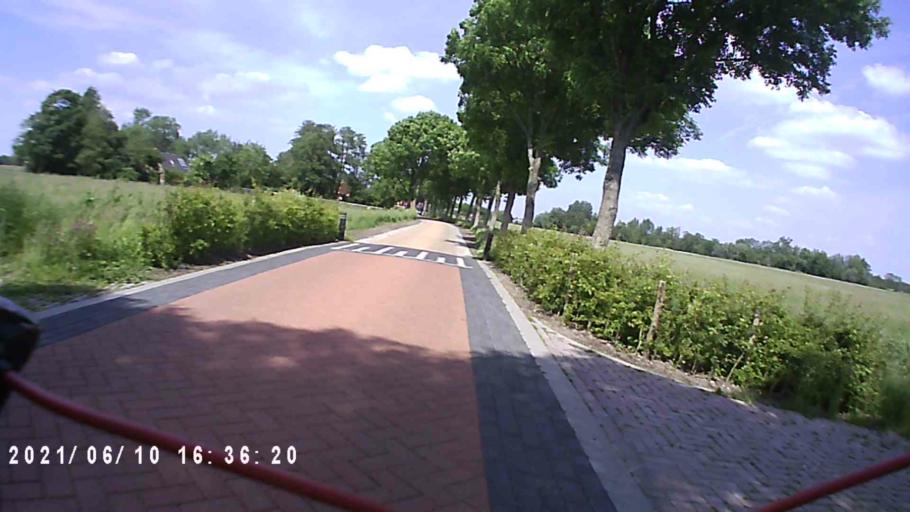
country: NL
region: Friesland
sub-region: Gemeente Achtkarspelen
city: Buitenpost
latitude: 53.2370
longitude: 6.1384
